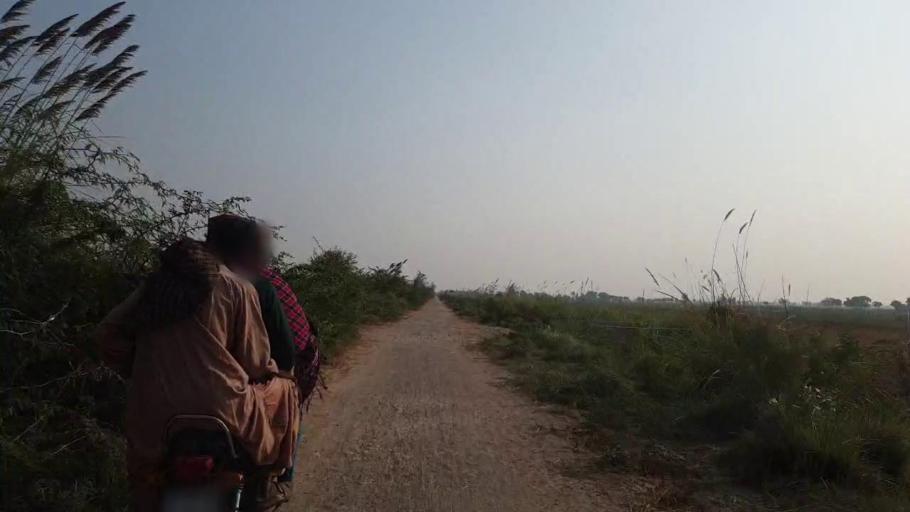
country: PK
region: Sindh
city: Tando Muhammad Khan
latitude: 25.0952
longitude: 68.3557
